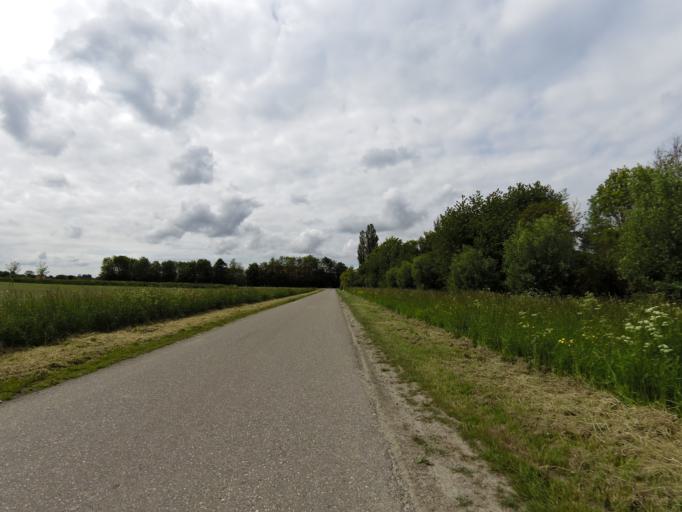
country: NL
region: South Holland
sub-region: Gemeente Hellevoetsluis
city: Nieuwenhoorn
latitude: 51.8798
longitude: 4.1362
